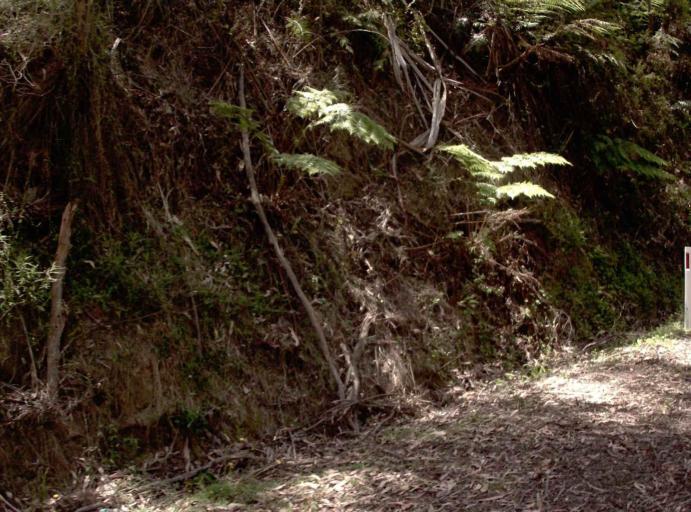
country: AU
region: New South Wales
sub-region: Bombala
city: Bombala
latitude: -37.4646
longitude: 148.9356
